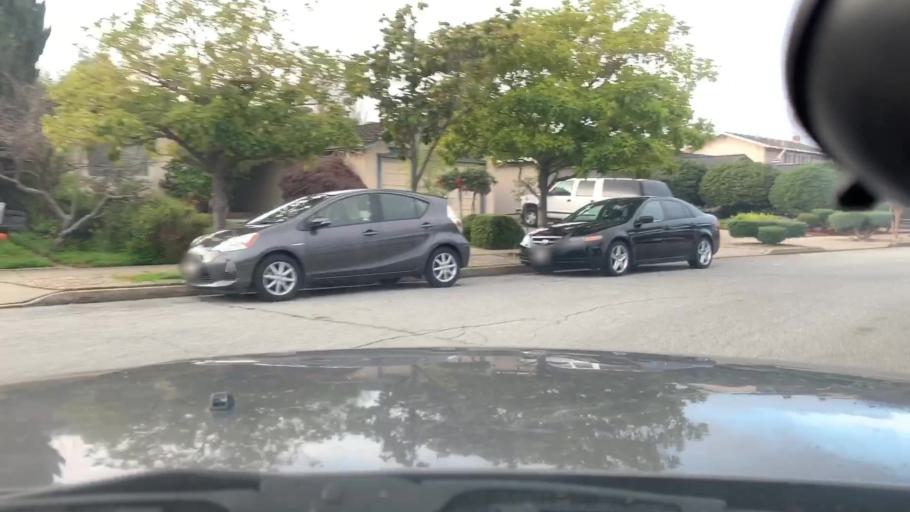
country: US
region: California
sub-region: Santa Clara County
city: Campbell
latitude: 37.3046
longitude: -121.9902
